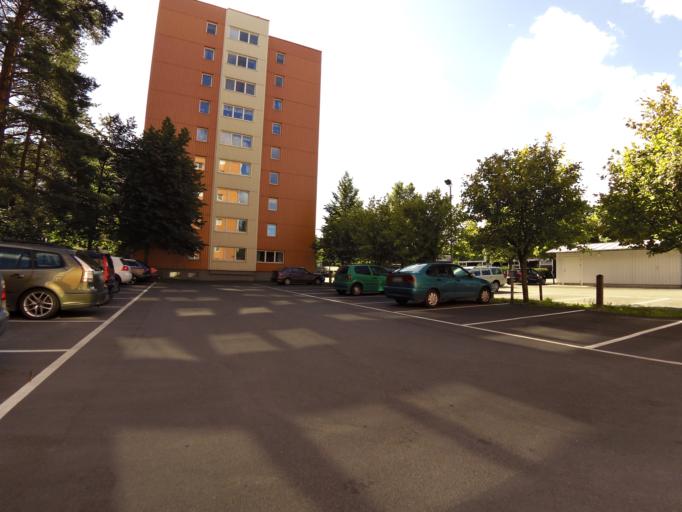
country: SE
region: Gaevleborg
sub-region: Gavle Kommun
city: Gavle
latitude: 60.6980
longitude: 17.1472
